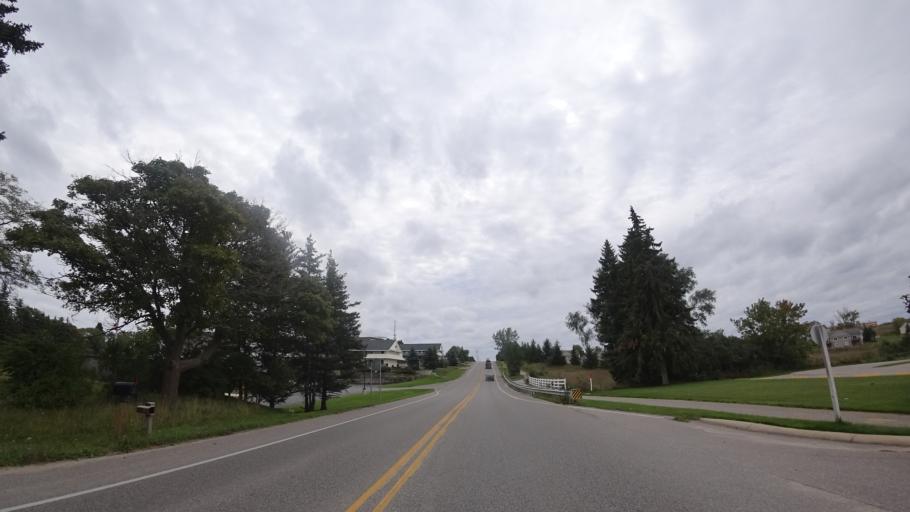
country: US
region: Michigan
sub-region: Emmet County
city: Petoskey
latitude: 45.3584
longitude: -84.9709
